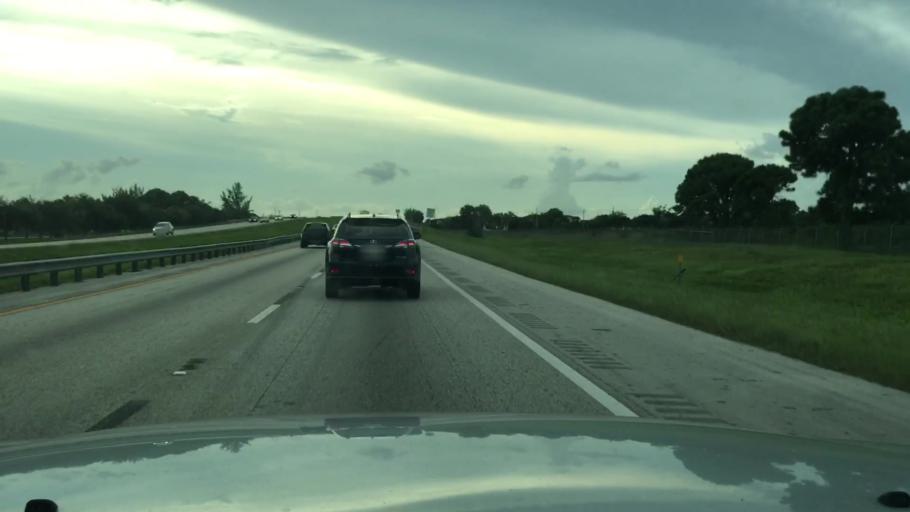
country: US
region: Florida
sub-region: Miami-Dade County
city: Lake Lucerne
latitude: 25.9722
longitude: -80.2580
